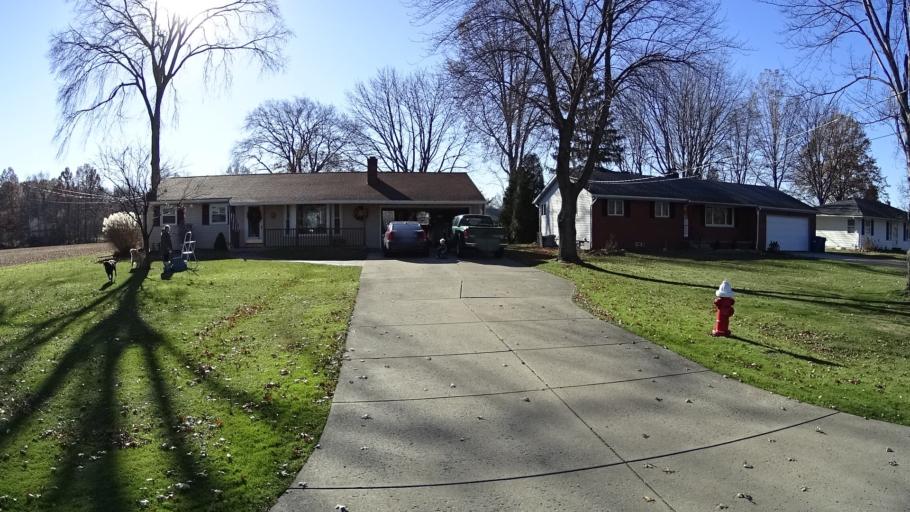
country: US
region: Ohio
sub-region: Lorain County
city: Avon
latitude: 41.4470
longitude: -82.0249
